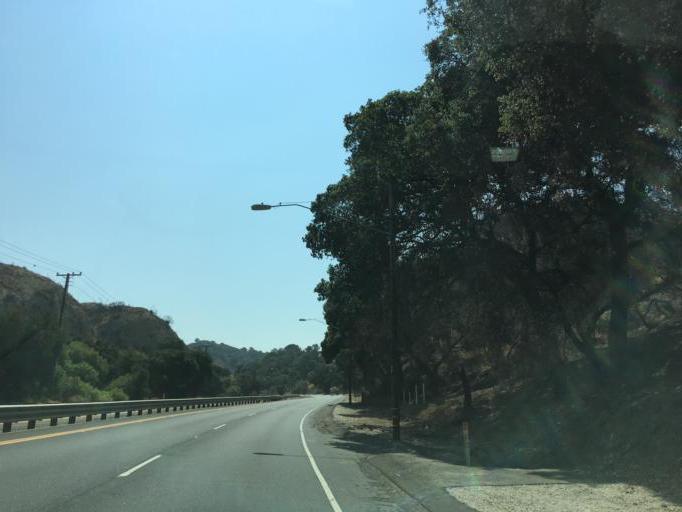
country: US
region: California
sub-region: Los Angeles County
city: Santa Clarita
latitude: 34.3498
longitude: -118.5386
